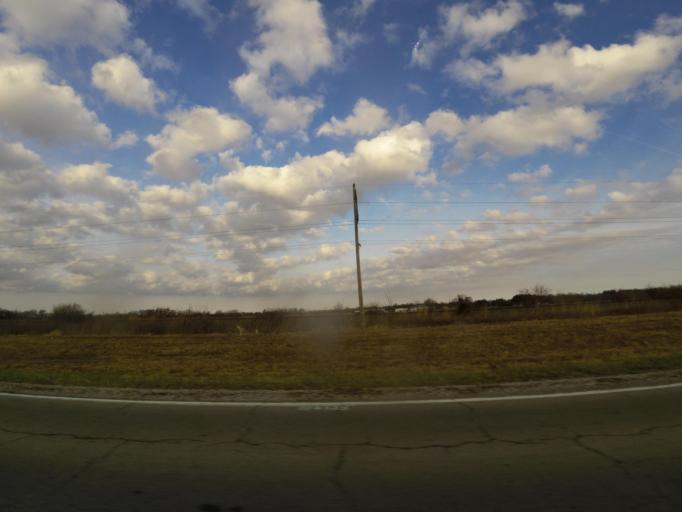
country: US
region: Illinois
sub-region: Bond County
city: Greenville
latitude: 38.9171
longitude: -89.2890
